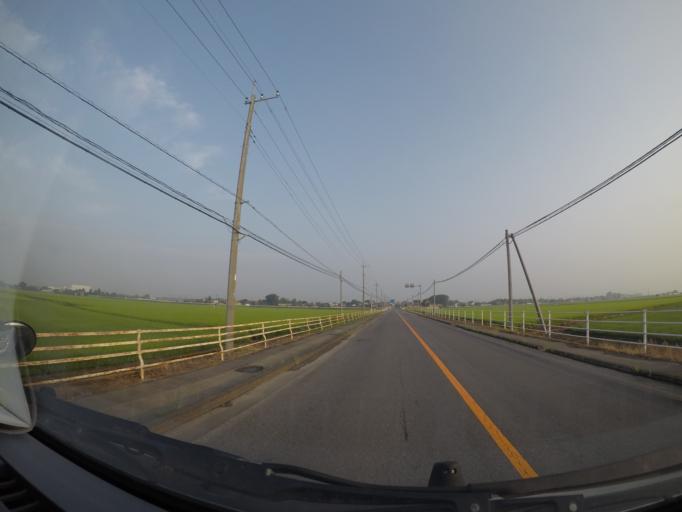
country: JP
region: Tochigi
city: Fujioka
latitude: 36.2767
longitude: 139.7109
